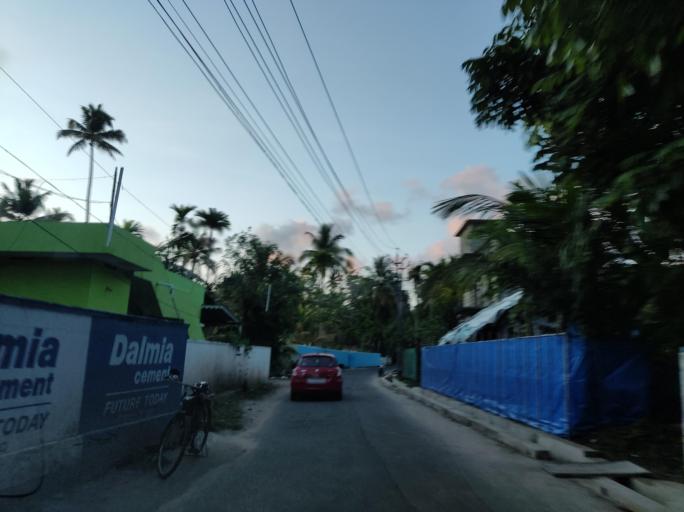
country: IN
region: Kerala
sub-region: Alappuzha
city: Vayalar
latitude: 9.7404
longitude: 76.2883
